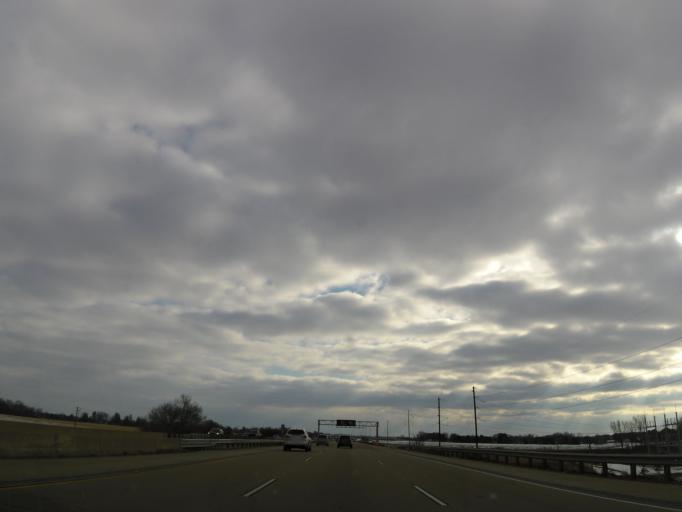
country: US
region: Wisconsin
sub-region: Dane County
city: Windsor
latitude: 43.2223
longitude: -89.3642
